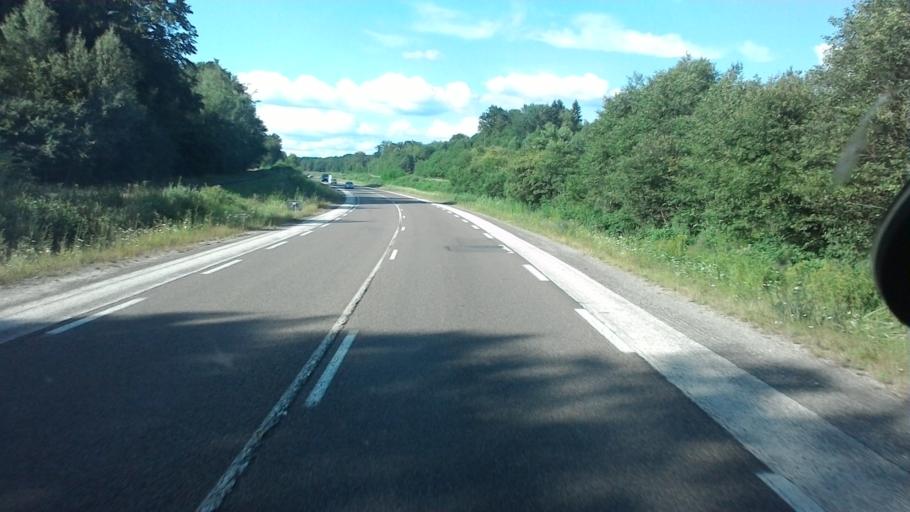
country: FR
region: Franche-Comte
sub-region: Departement de la Haute-Saone
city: Saint-Sauveur
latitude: 47.7917
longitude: 6.4003
